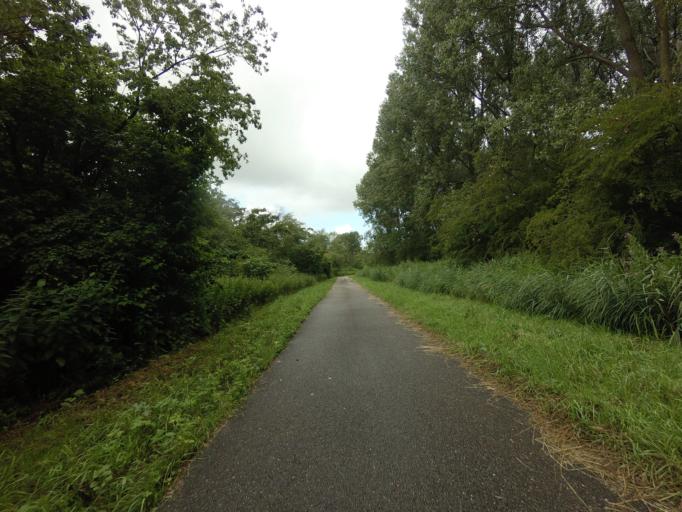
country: NL
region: North Holland
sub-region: Gemeente Velsen
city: Velsen-Zuid
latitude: 52.4374
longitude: 4.6954
